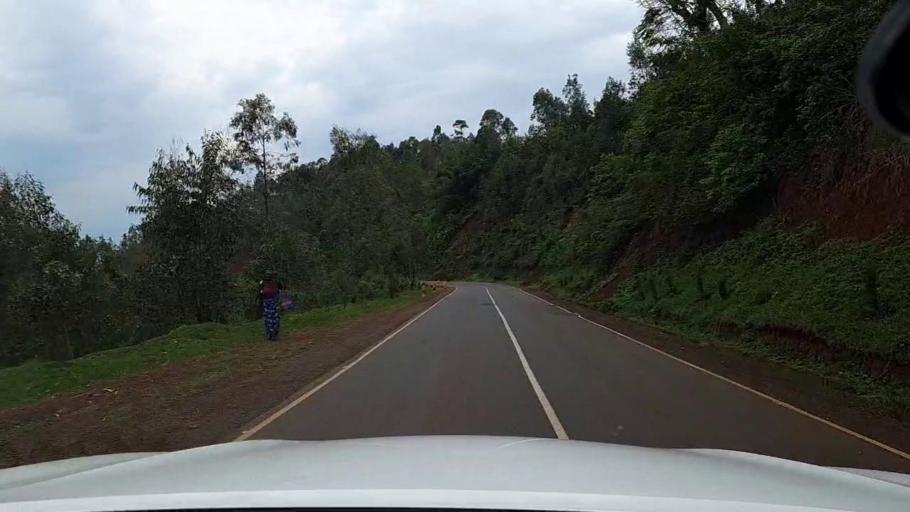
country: RW
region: Western Province
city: Cyangugu
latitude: -2.6464
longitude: 28.9633
